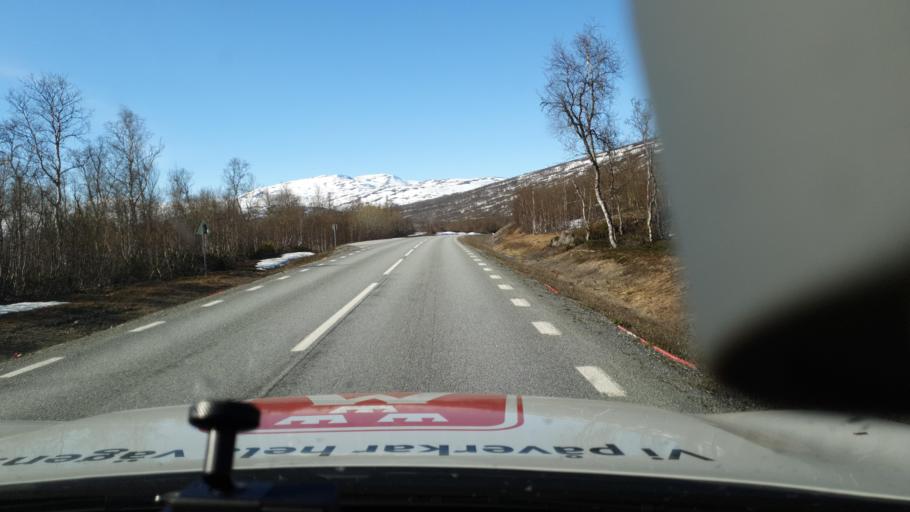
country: NO
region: Nordland
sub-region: Rana
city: Mo i Rana
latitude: 66.0619
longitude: 14.8723
